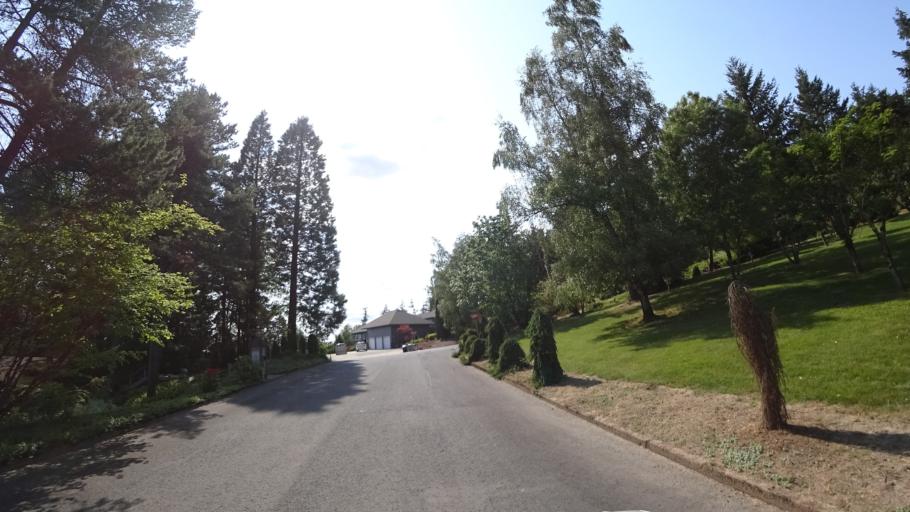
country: US
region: Oregon
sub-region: Clackamas County
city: Happy Valley
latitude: 45.4410
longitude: -122.5456
